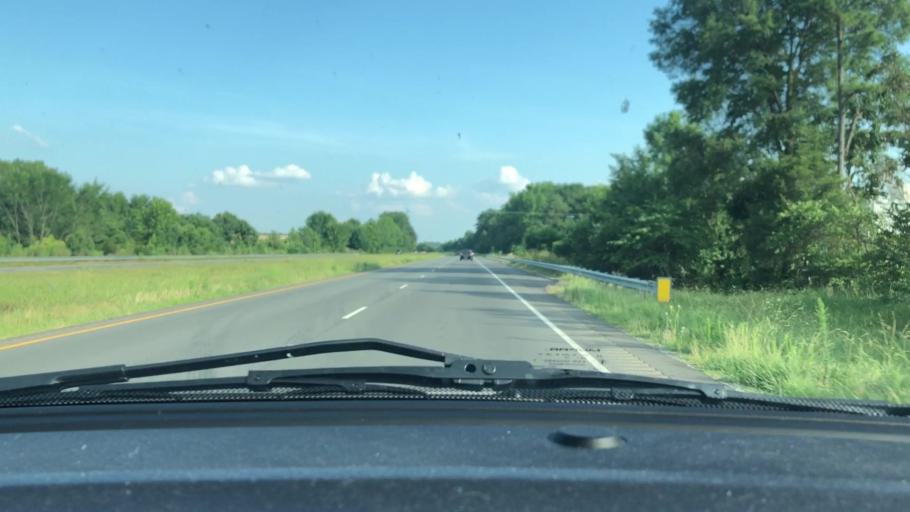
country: US
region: North Carolina
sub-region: Chatham County
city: Siler City
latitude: 35.6744
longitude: -79.4132
